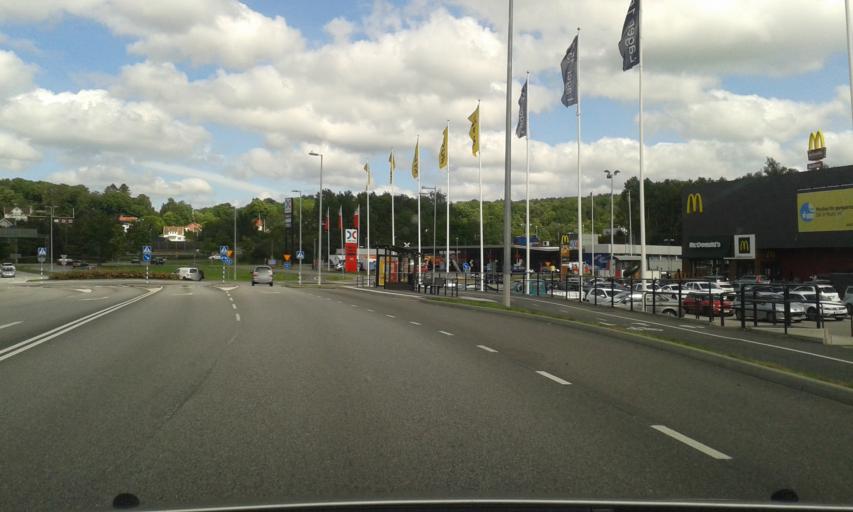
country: SE
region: Vaestra Goetaland
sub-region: Molndal
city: Kallered
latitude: 57.6013
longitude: 12.0495
